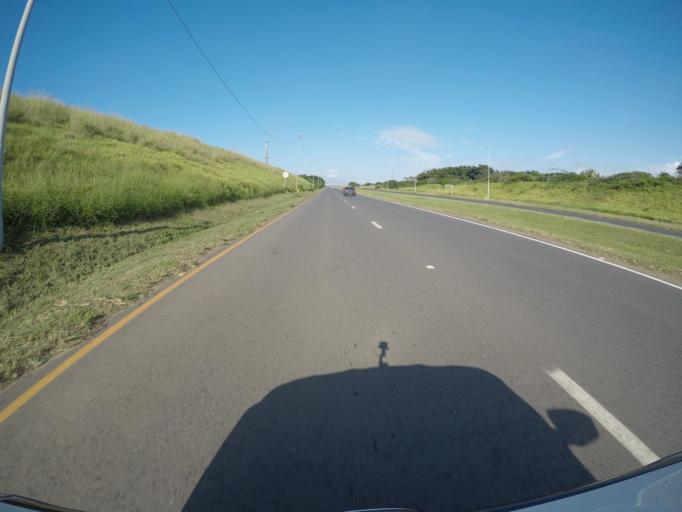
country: ZA
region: KwaZulu-Natal
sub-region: uThungulu District Municipality
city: Richards Bay
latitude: -28.7694
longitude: 32.0417
